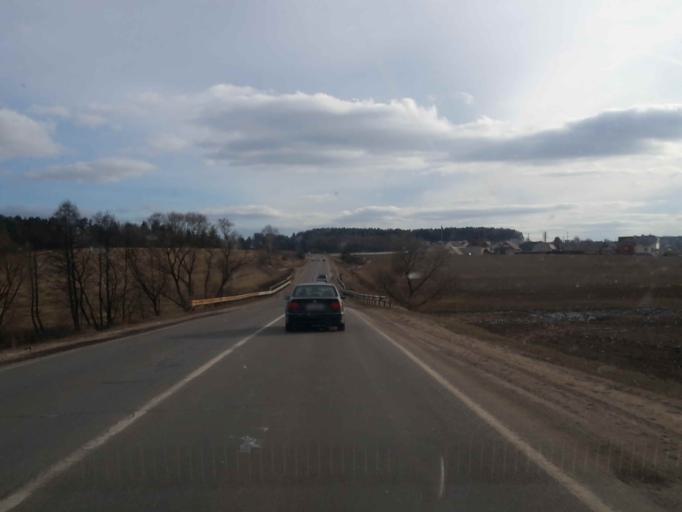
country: BY
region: Minsk
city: Bal'shavik
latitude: 54.0371
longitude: 27.5612
